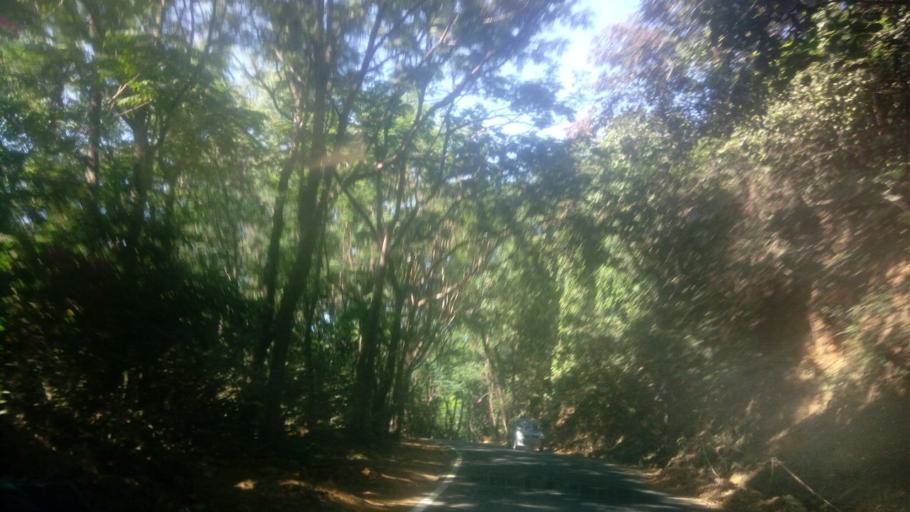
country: IN
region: Goa
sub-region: North Goa
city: Valpoy
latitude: 15.6128
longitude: 74.1192
